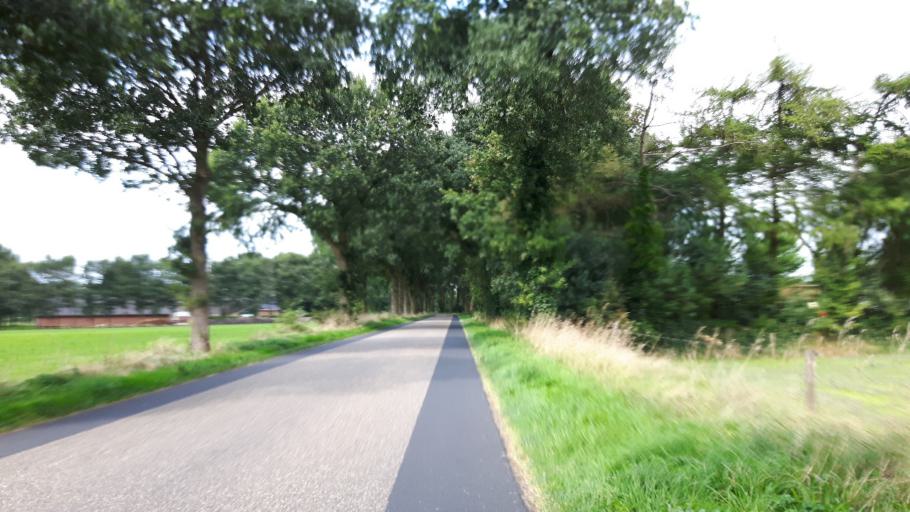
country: NL
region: Groningen
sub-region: Gemeente Leek
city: Leek
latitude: 53.0861
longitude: 6.3182
